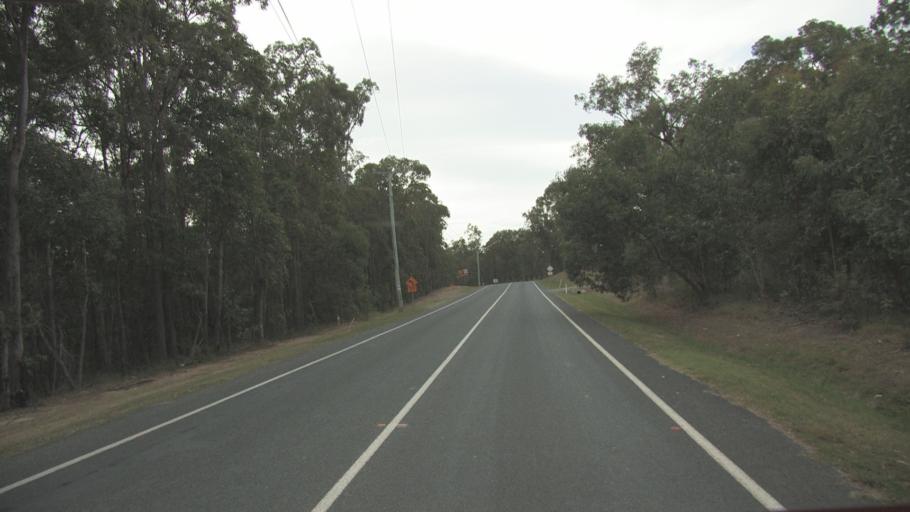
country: AU
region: Queensland
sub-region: Logan
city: Windaroo
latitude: -27.7227
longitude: 153.1598
